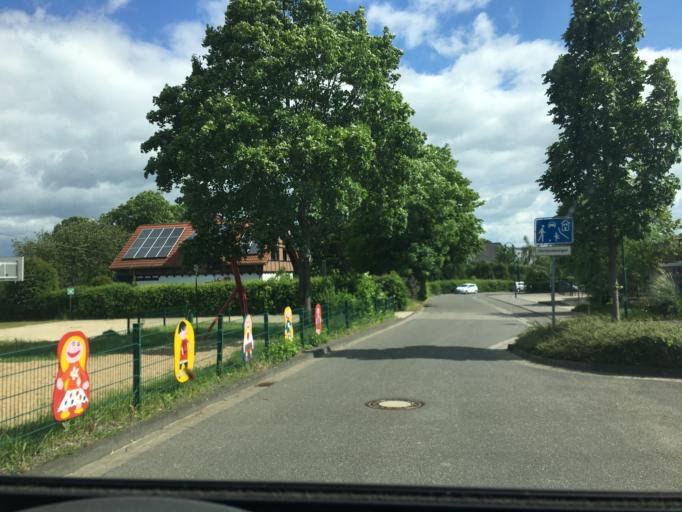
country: DE
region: North Rhine-Westphalia
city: Meckenheim
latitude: 50.5847
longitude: 7.0317
